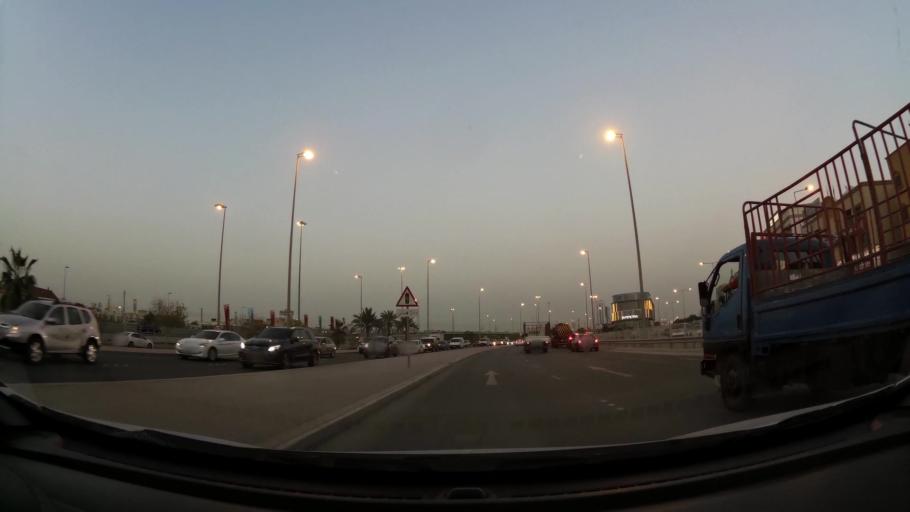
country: BH
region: Manama
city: Jidd Hafs
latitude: 26.2034
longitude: 50.5638
